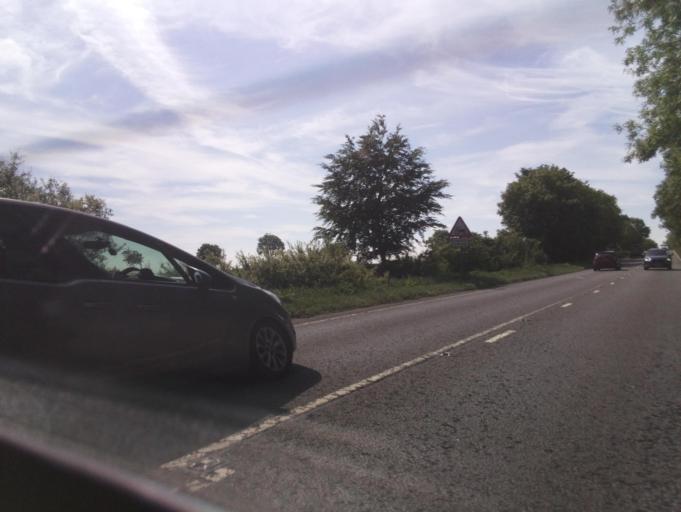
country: GB
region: England
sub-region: Lincolnshire
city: Burton
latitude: 53.3497
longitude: -0.5447
